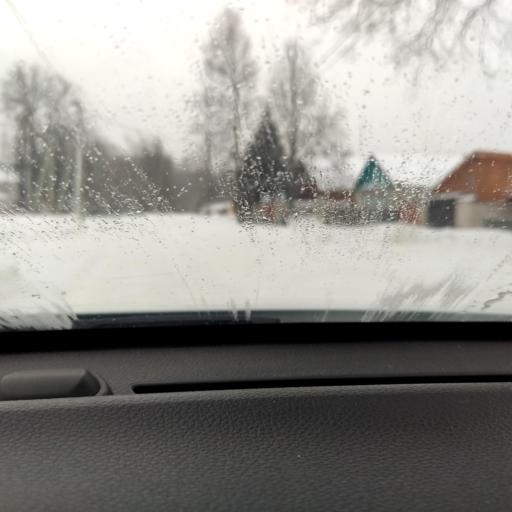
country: RU
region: Tatarstan
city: Stolbishchi
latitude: 55.6734
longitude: 49.1134
